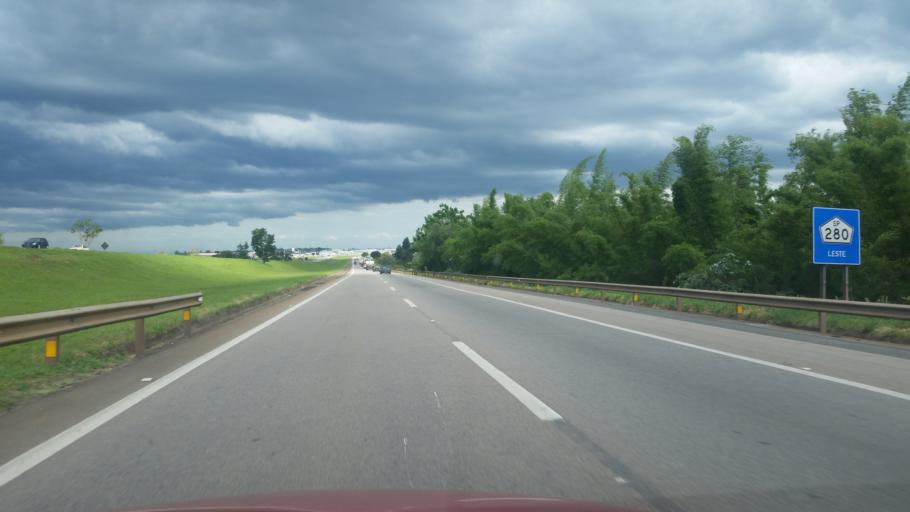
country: BR
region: Sao Paulo
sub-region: Boituva
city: Boituva
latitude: -23.2984
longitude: -47.6770
